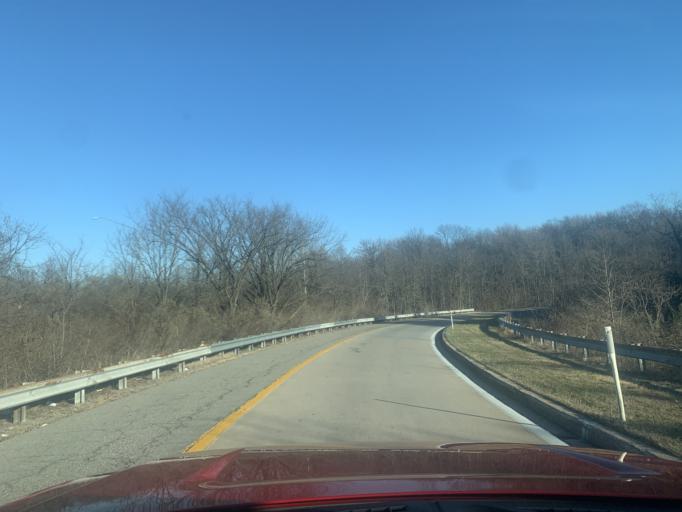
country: US
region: Maryland
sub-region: Anne Arundel County
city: Brooklyn Park
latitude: 39.2084
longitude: -76.6018
